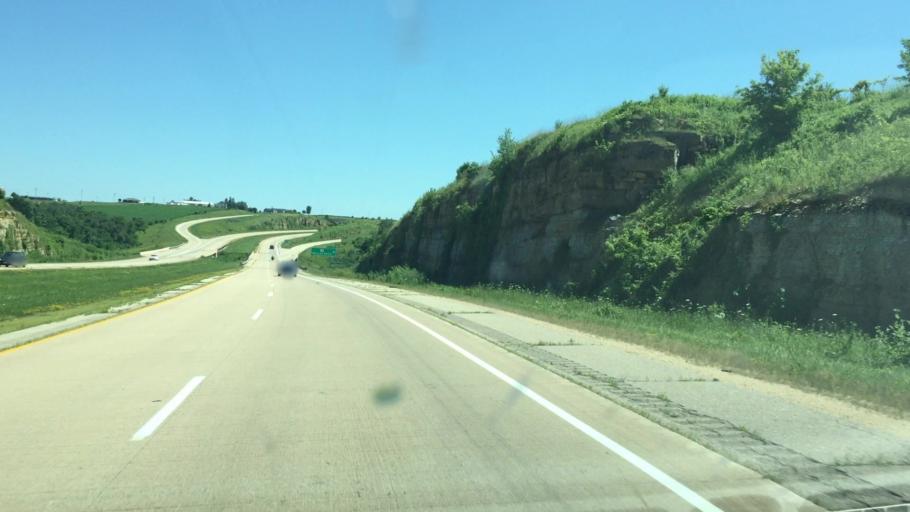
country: US
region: Wisconsin
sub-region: Iowa County
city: Mineral Point
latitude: 42.8560
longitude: -90.2026
